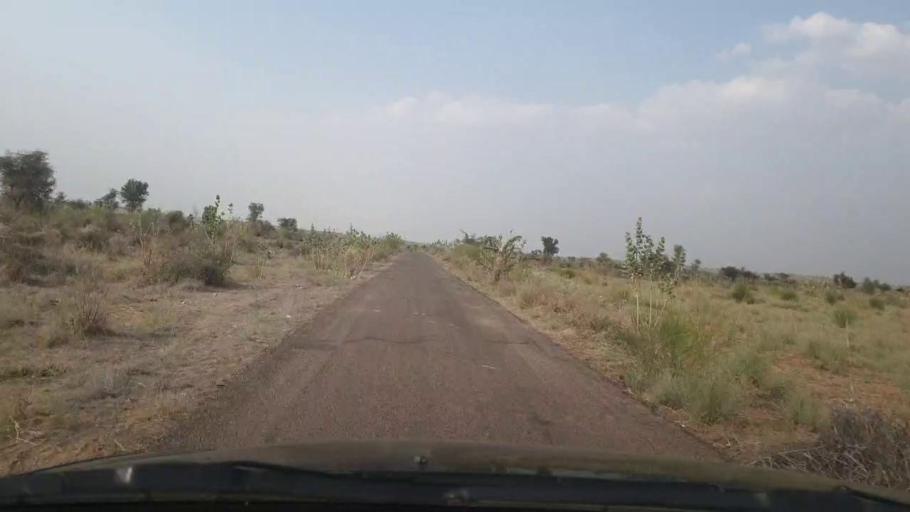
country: PK
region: Sindh
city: Islamkot
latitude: 25.0550
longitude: 70.5598
